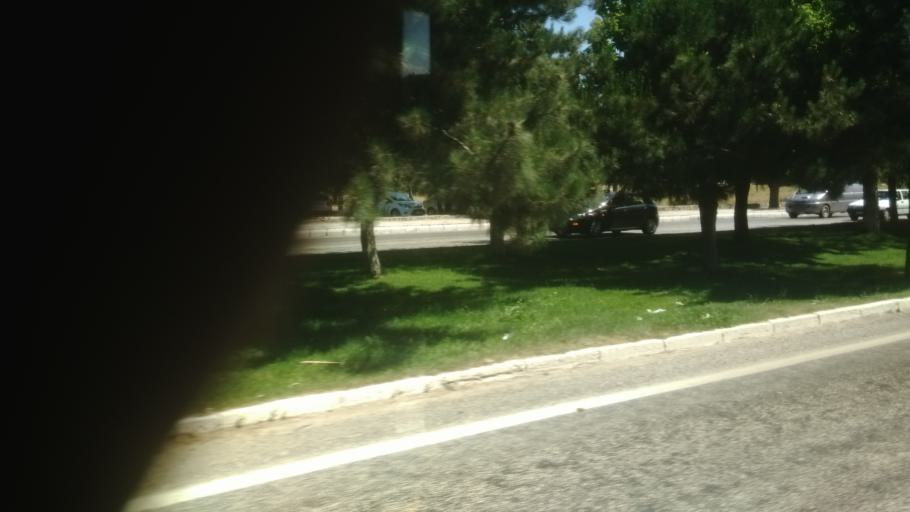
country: TR
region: Isparta
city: Isparta
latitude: 37.7823
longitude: 30.5667
